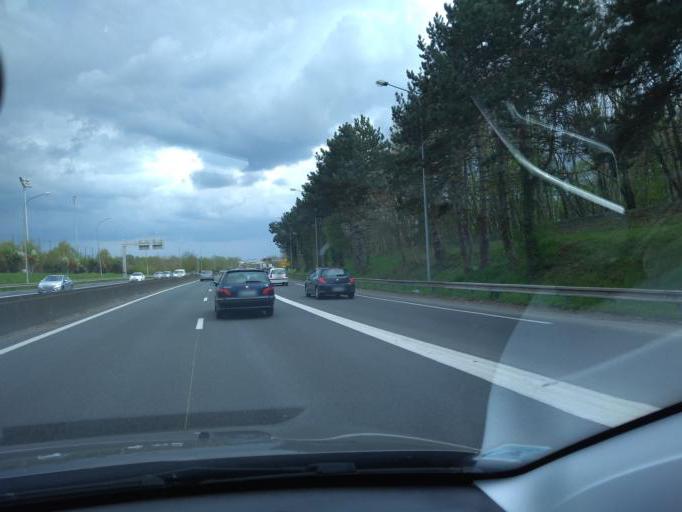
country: FR
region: Pays de la Loire
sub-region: Departement de Maine-et-Loire
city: Avrille
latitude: 47.4686
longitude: -0.5870
